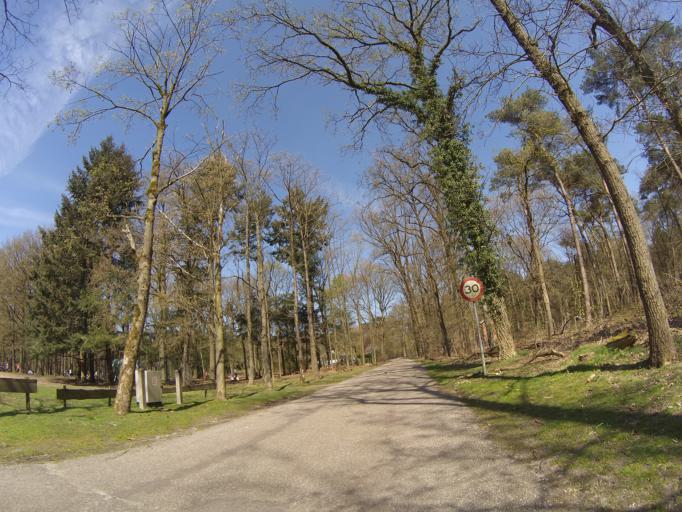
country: NL
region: Utrecht
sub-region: Gemeente Utrechtse Heuvelrug
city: Driebergen-Rijsenburg
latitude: 52.0928
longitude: 5.2979
